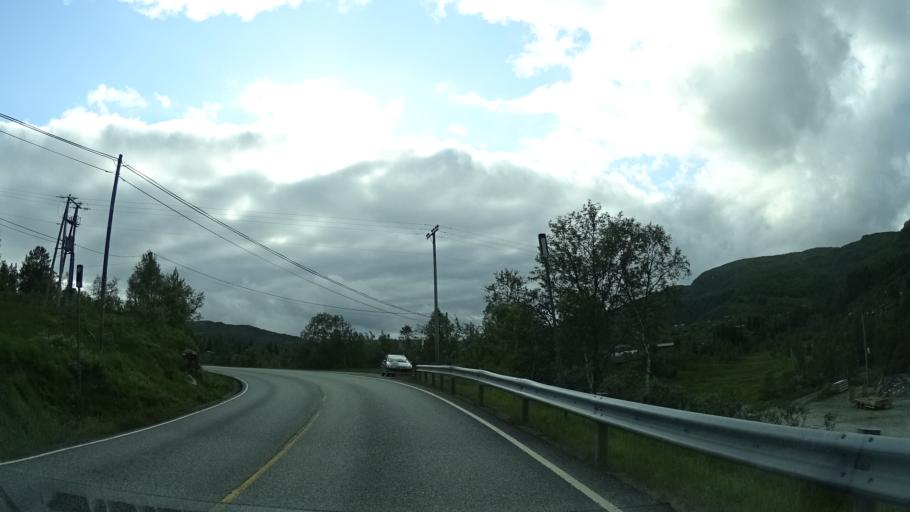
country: NO
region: Hordaland
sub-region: Kvam
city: Norheimsund
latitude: 60.3882
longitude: 5.9754
